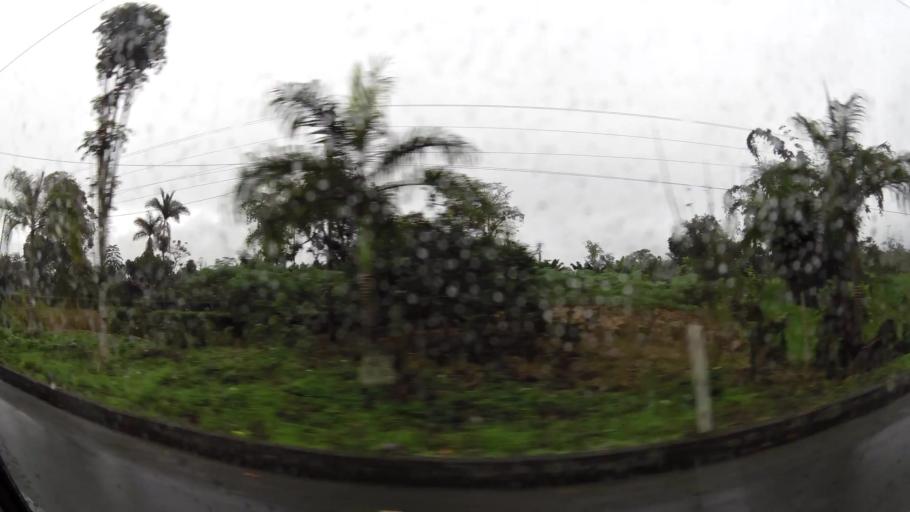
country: EC
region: Santo Domingo de los Tsachilas
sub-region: Canton Santo Domingo de los Colorados
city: Santo Domingo de los Colorados
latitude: -0.2285
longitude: -79.1243
